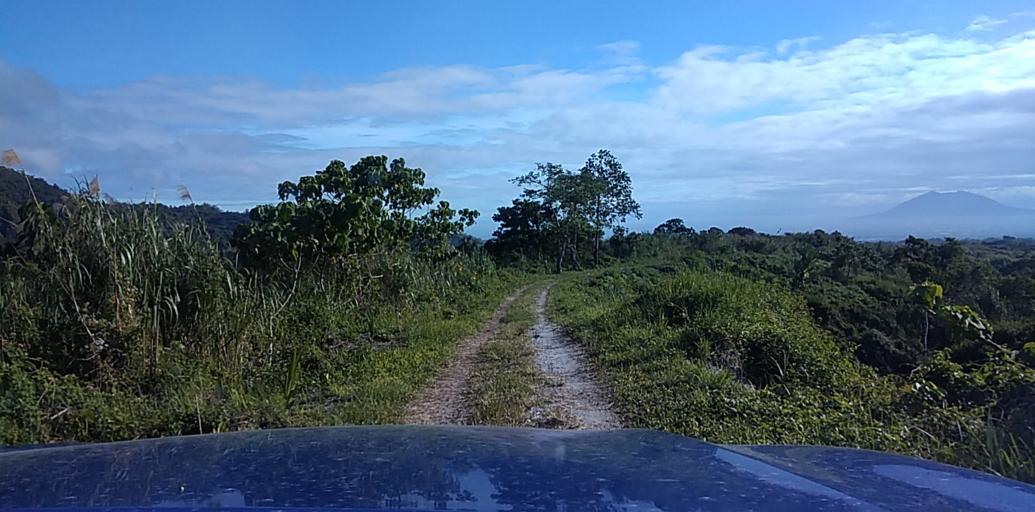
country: PH
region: Central Luzon
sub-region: Province of Pampanga
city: Babo-Pangulo
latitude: 15.1488
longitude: 120.4276
